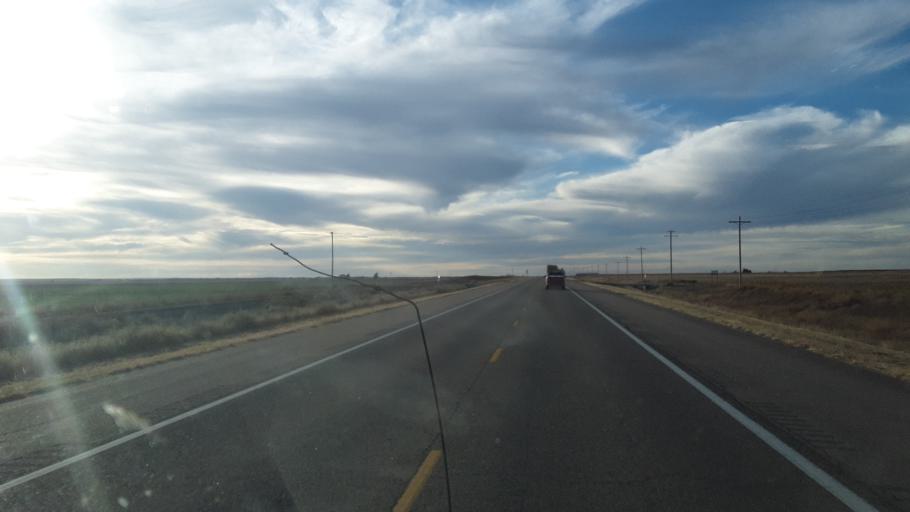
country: US
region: Kansas
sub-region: Hamilton County
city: Syracuse
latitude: 37.9503
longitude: -101.6126
